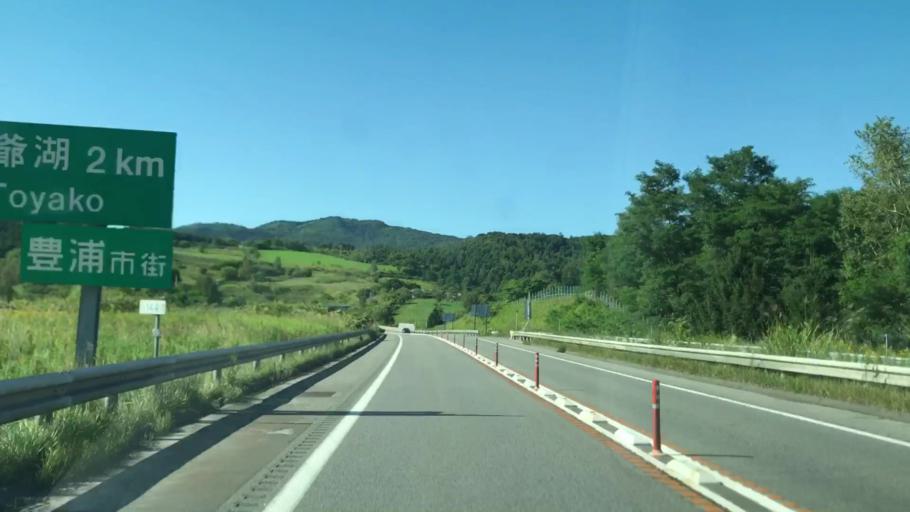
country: JP
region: Hokkaido
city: Date
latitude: 42.5484
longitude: 140.7914
